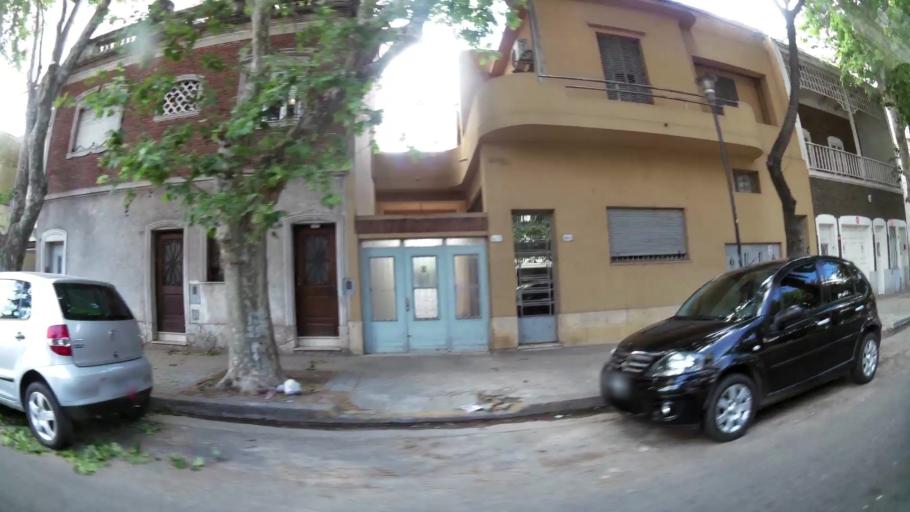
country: AR
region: Santa Fe
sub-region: Departamento de Rosario
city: Rosario
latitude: -32.9326
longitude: -60.6503
